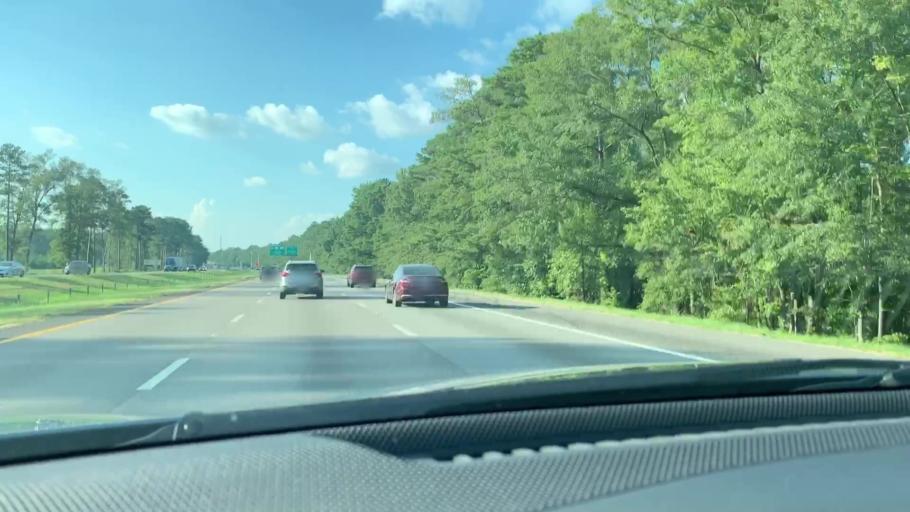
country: US
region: South Carolina
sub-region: Lexington County
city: Pineridge
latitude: 33.9067
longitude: -81.0523
